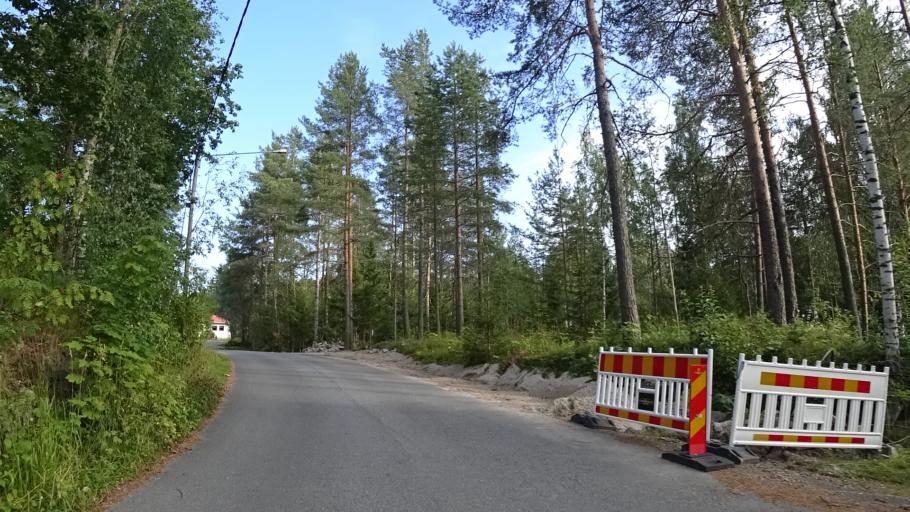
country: FI
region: North Karelia
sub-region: Joensuu
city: Eno
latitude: 62.8014
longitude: 30.1597
